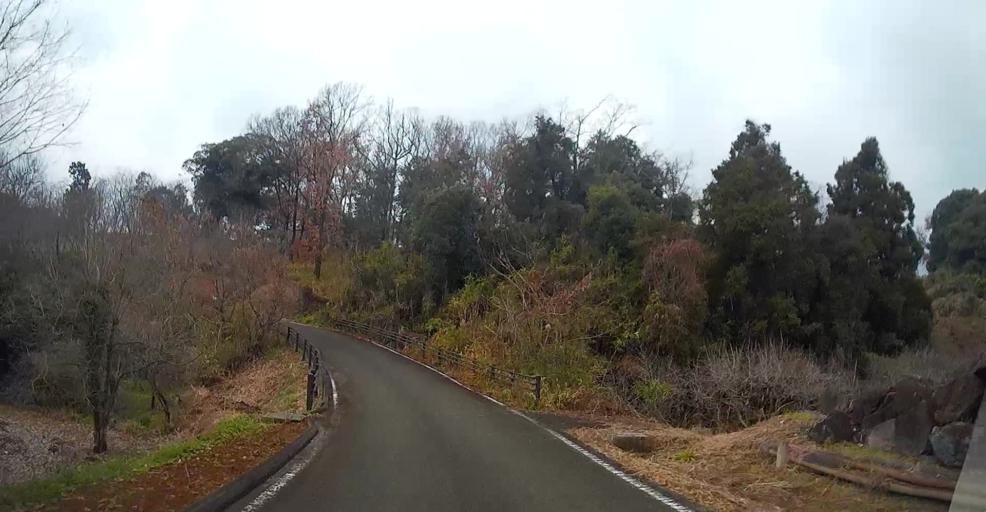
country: JP
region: Kumamoto
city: Matsubase
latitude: 32.6452
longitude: 130.7389
